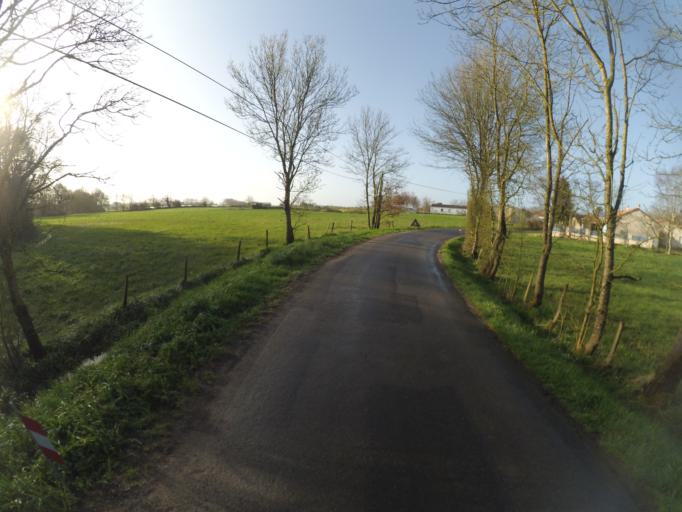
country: FR
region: Pays de la Loire
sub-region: Departement de la Loire-Atlantique
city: La Planche
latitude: 47.0231
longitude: -1.4546
